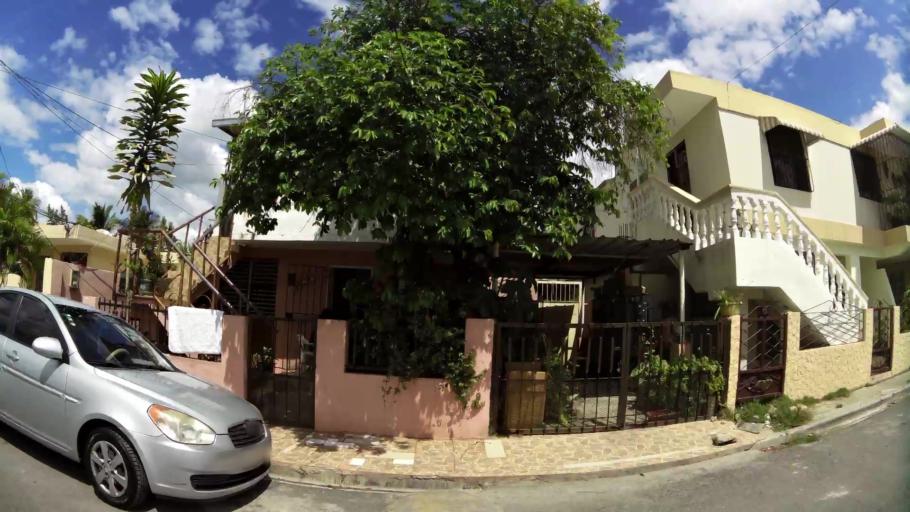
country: DO
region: Nacional
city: Ensanche Luperon
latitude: 18.5263
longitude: -69.8989
